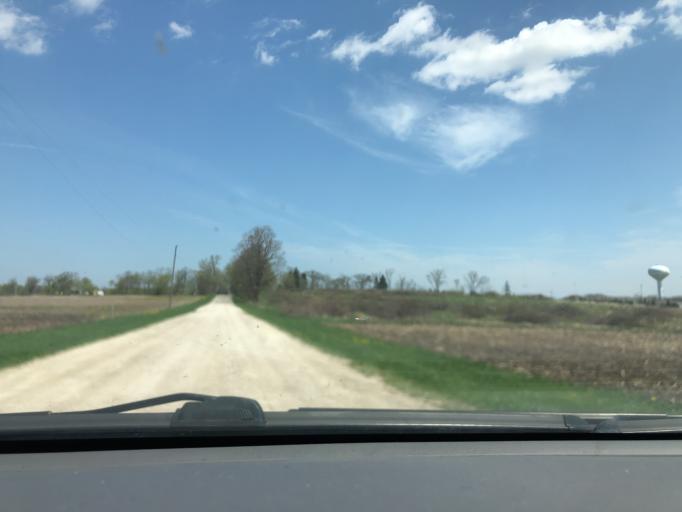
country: US
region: Illinois
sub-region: Kane County
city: Pingree Grove
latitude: 42.0813
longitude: -88.4635
